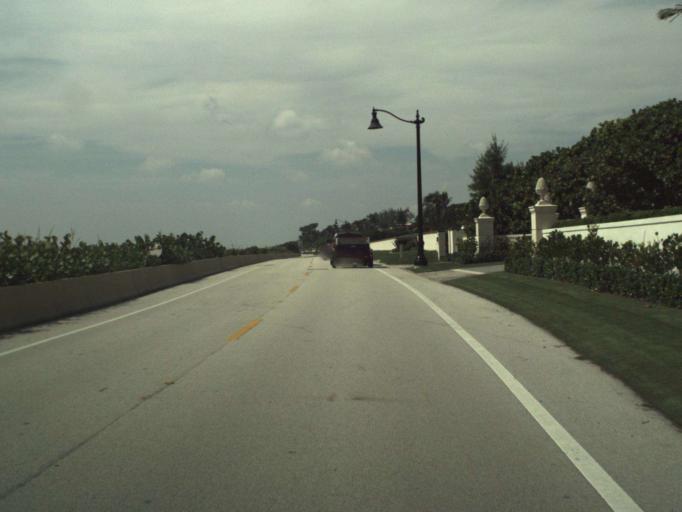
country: US
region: Florida
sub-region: Palm Beach County
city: Lake Clarke Shores
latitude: 26.6524
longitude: -80.0371
